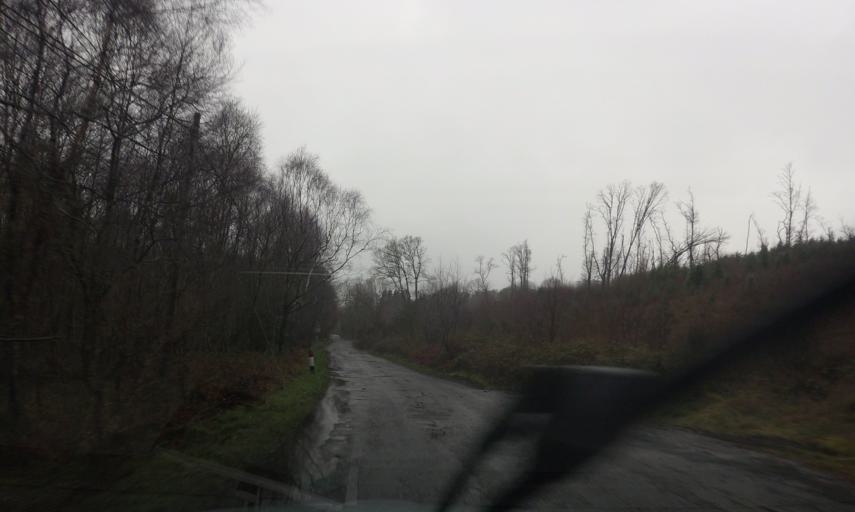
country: GB
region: Scotland
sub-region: West Dunbartonshire
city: Balloch
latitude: 56.1318
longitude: -4.6104
